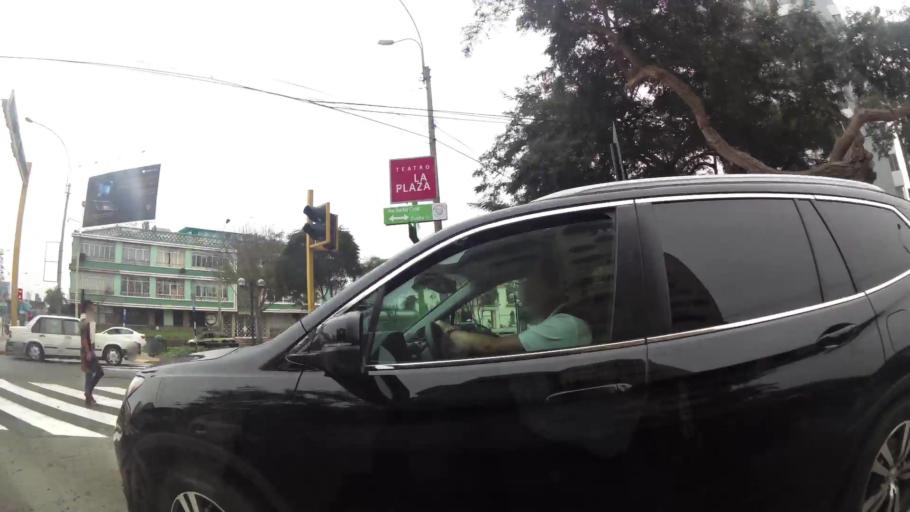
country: PE
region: Lima
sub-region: Lima
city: San Isidro
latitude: -12.1037
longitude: -77.0318
